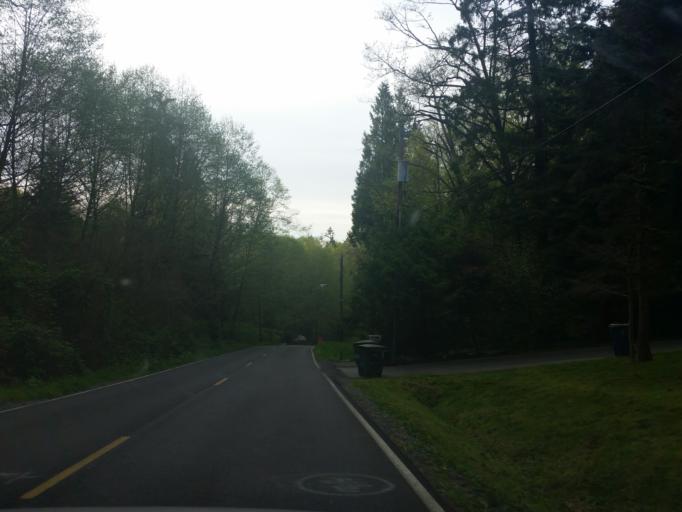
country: US
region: Washington
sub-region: Snohomish County
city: Meadowdale
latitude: 47.8442
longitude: -122.3300
